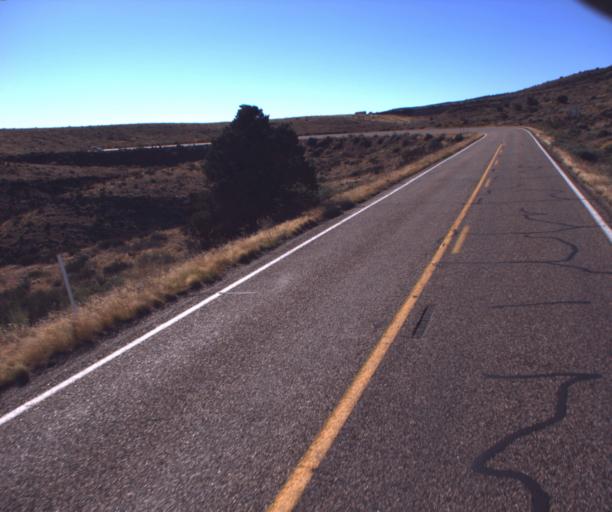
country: US
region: Arizona
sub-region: Coconino County
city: Fredonia
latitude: 36.7281
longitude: -112.0621
